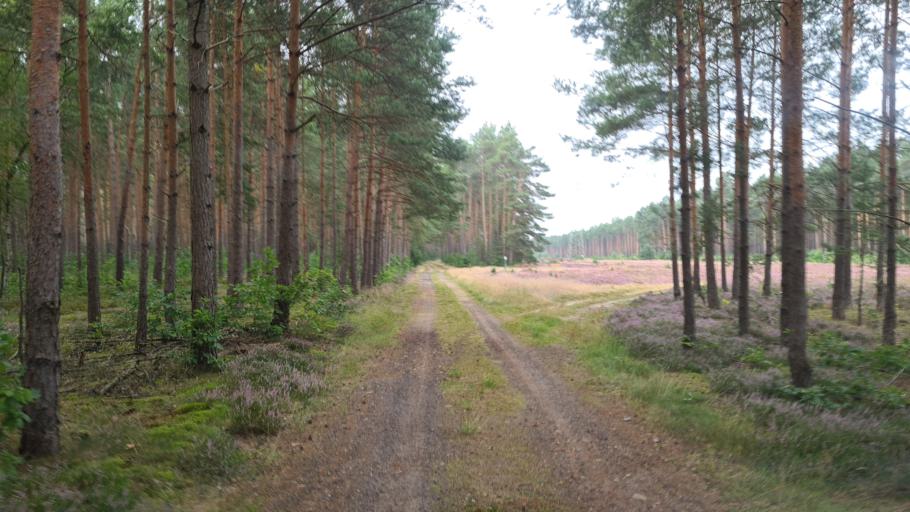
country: DE
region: Brandenburg
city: Hohenbucko
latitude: 51.7713
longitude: 13.5573
